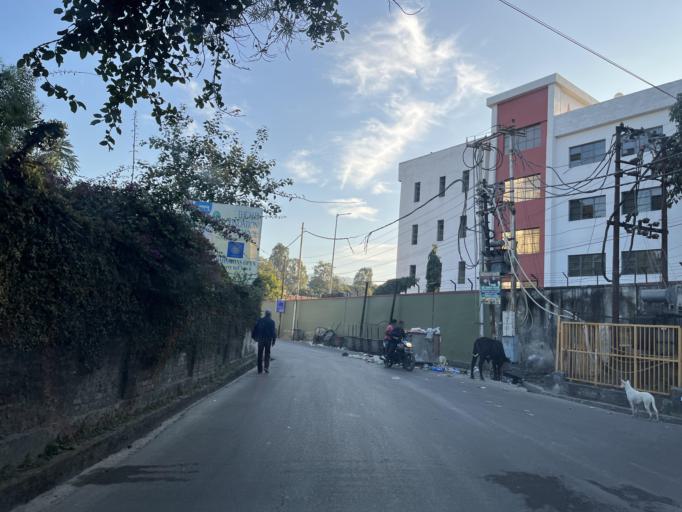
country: IN
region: Uttarakhand
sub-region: Naini Tal
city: Haldwani
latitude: 29.2168
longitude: 79.5265
